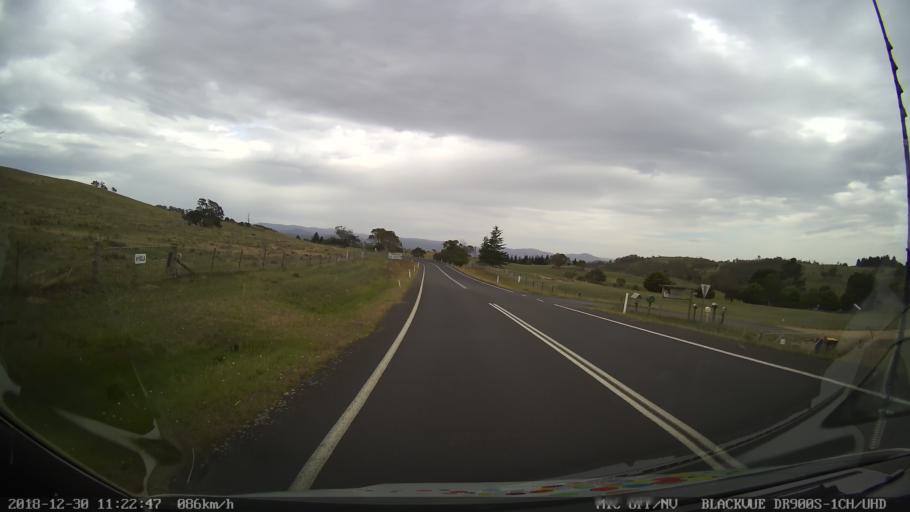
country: AU
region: New South Wales
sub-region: Snowy River
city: Jindabyne
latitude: -36.4953
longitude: 148.6703
